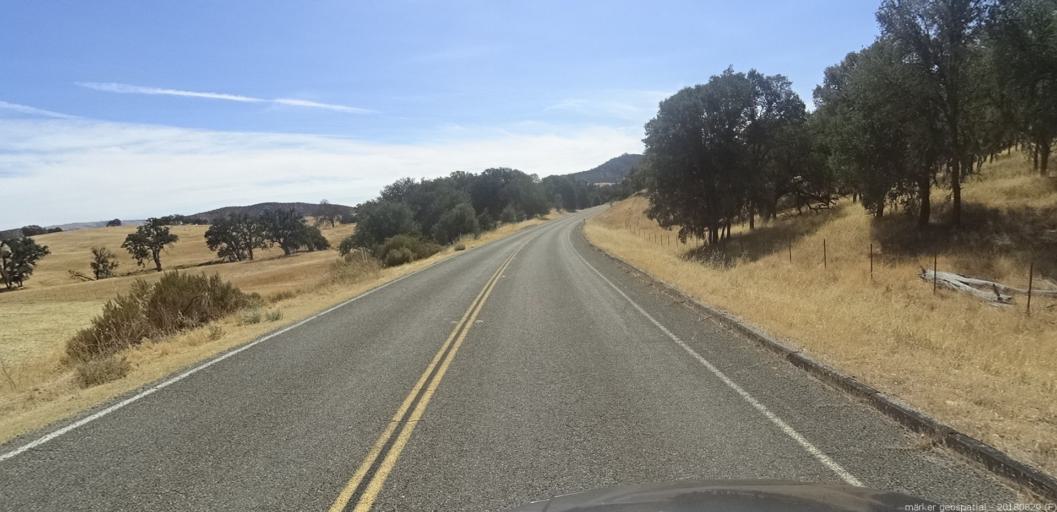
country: US
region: California
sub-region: San Luis Obispo County
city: Lake Nacimiento
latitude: 35.8084
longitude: -120.9976
